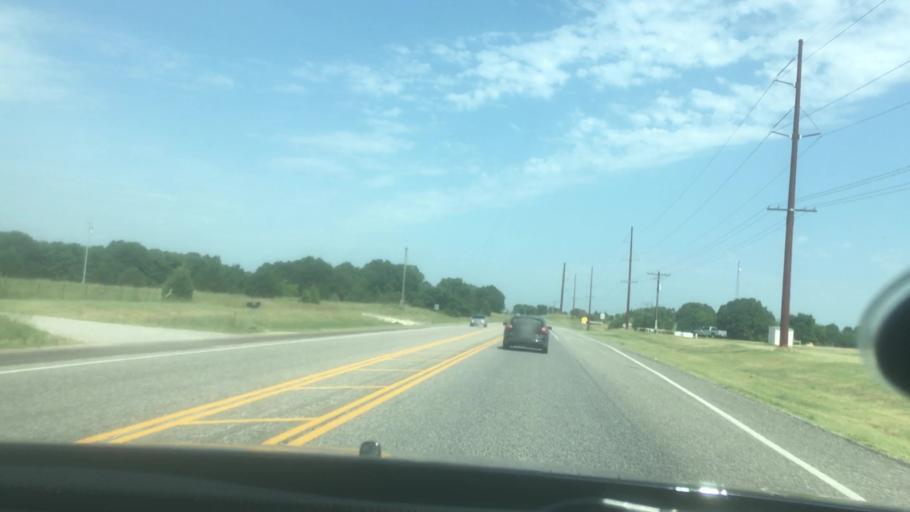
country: US
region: Oklahoma
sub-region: Seminole County
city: Konawa
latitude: 34.8644
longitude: -96.8291
